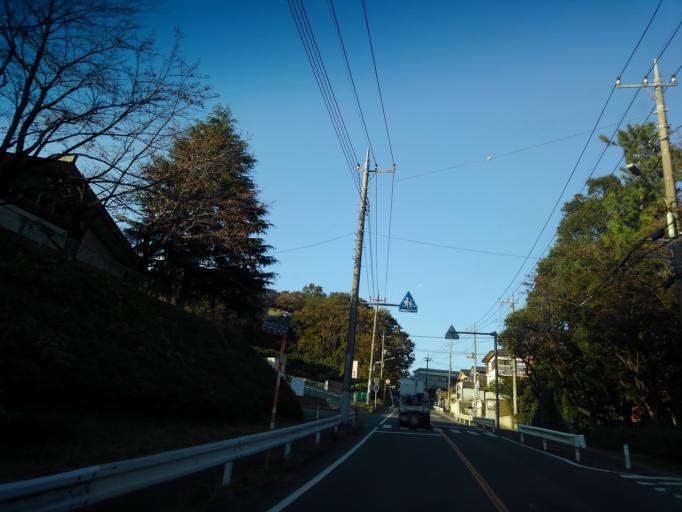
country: JP
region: Saitama
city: Tokorozawa
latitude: 35.7795
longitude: 139.4266
